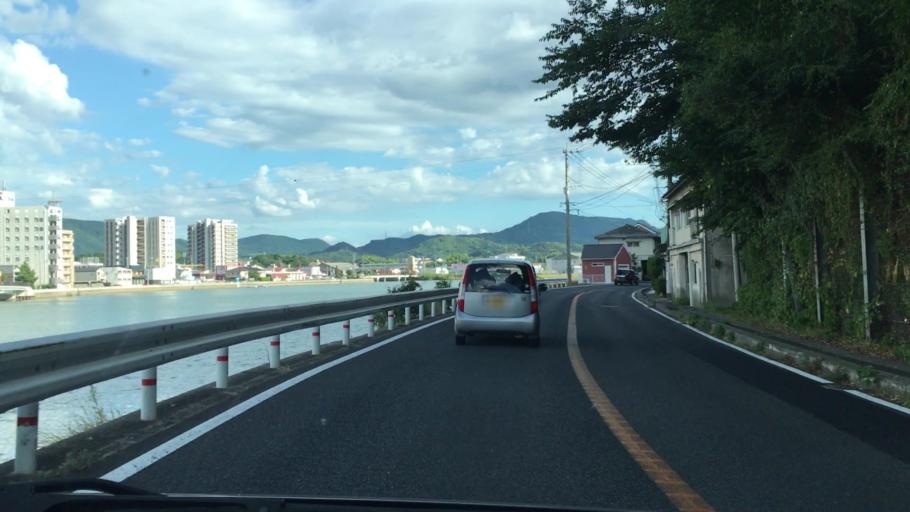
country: JP
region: Nagasaki
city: Sasebo
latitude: 33.1358
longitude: 129.7950
